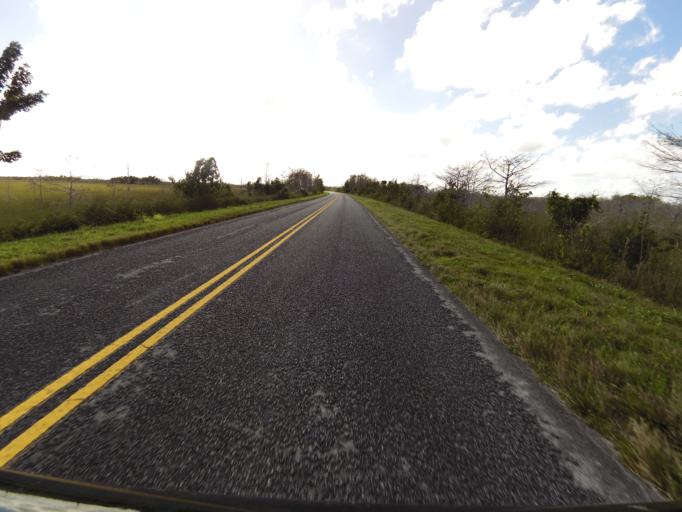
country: US
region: Florida
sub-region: Miami-Dade County
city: Florida City
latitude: 25.4242
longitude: -80.7750
